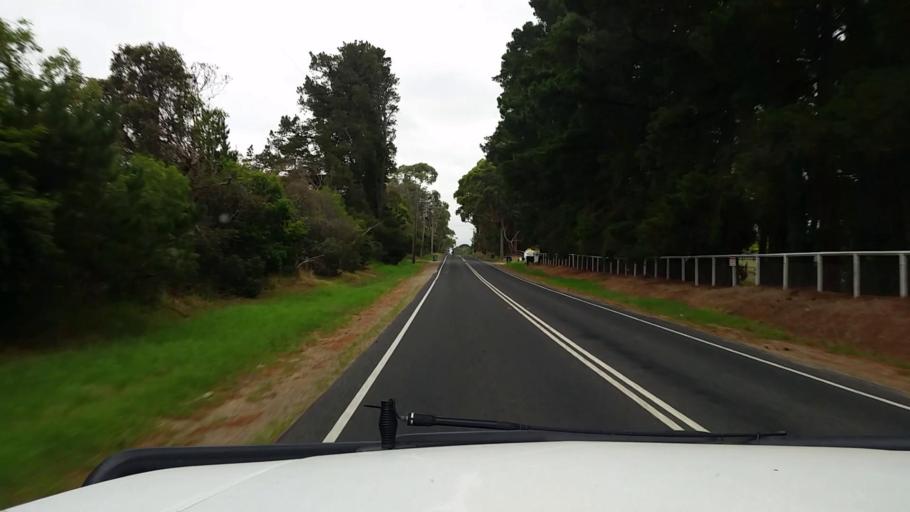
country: AU
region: Victoria
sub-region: Mornington Peninsula
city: Hastings
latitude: -38.2819
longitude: 145.1456
